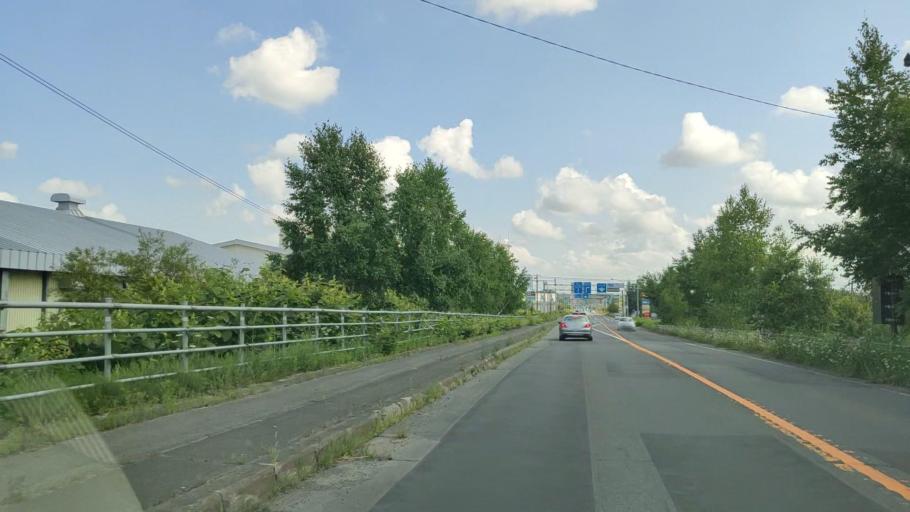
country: JP
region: Hokkaido
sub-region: Asahikawa-shi
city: Asahikawa
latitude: 43.5893
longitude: 142.4517
